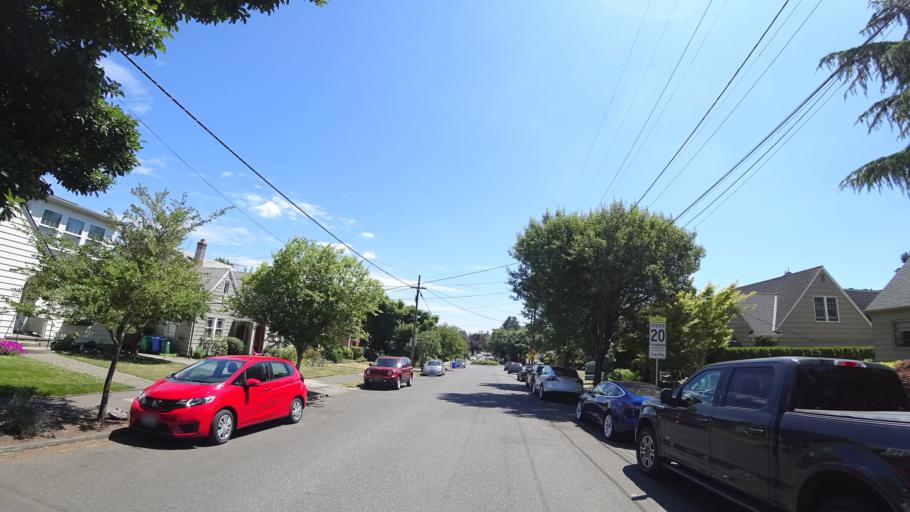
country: US
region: Oregon
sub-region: Multnomah County
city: Portland
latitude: 45.5339
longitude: -122.7079
